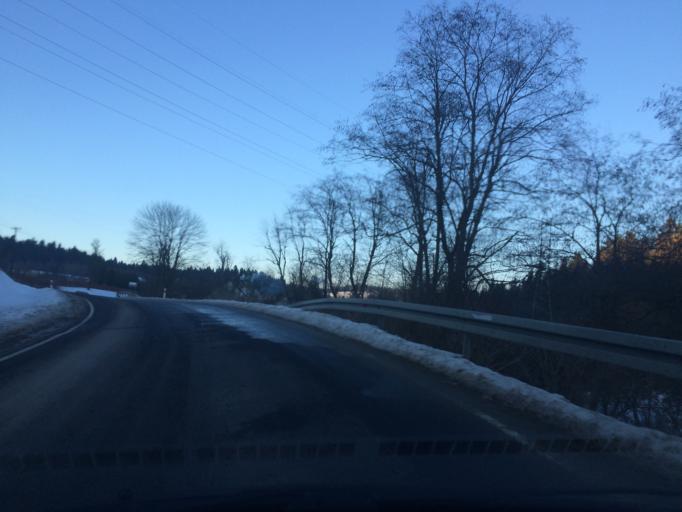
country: PL
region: Subcarpathian Voivodeship
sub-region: Powiat bieszczadzki
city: Lutowiska
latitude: 49.2201
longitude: 22.6938
